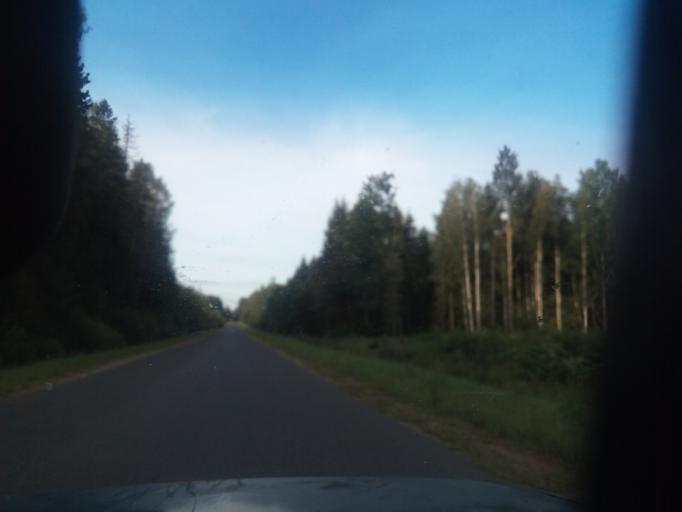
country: BY
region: Vitebsk
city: Dzisna
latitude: 55.6483
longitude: 28.3222
